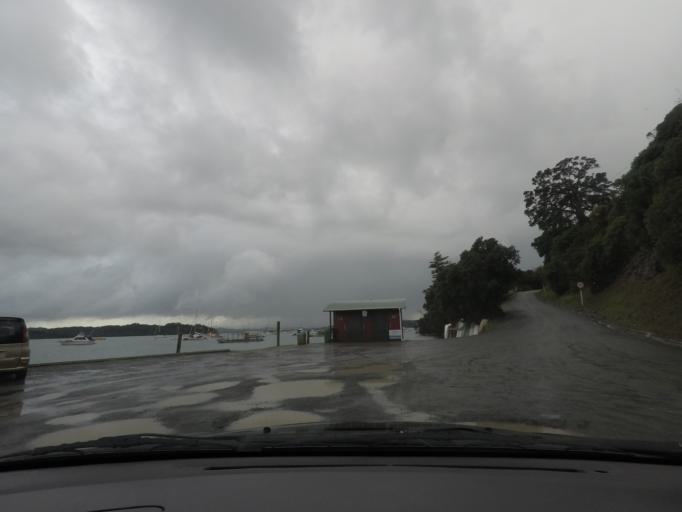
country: NZ
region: Auckland
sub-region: Auckland
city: Warkworth
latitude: -36.4857
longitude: 174.7239
